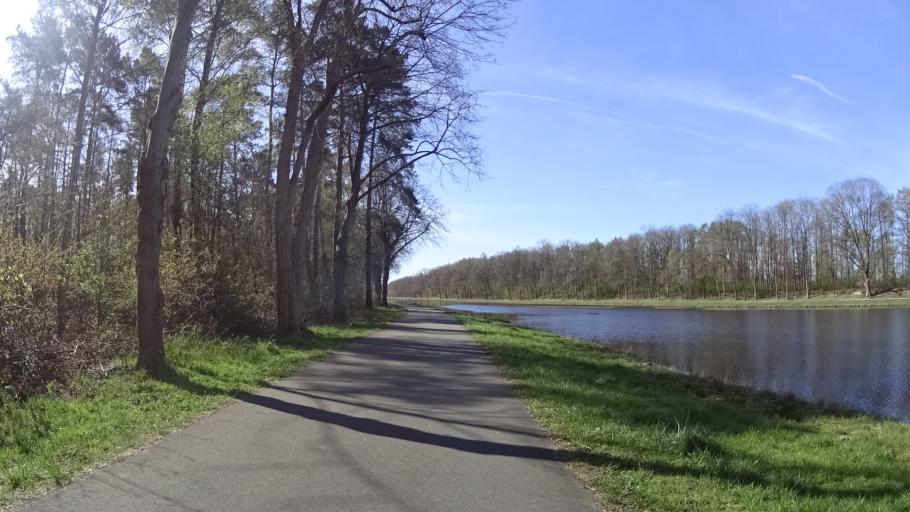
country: DE
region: Lower Saxony
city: Meppen
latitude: 52.6691
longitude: 7.3049
